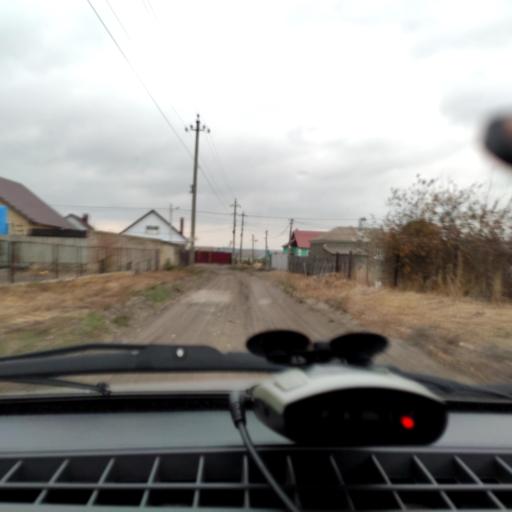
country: RU
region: Voronezj
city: Pridonskoy
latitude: 51.7046
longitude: 39.0689
